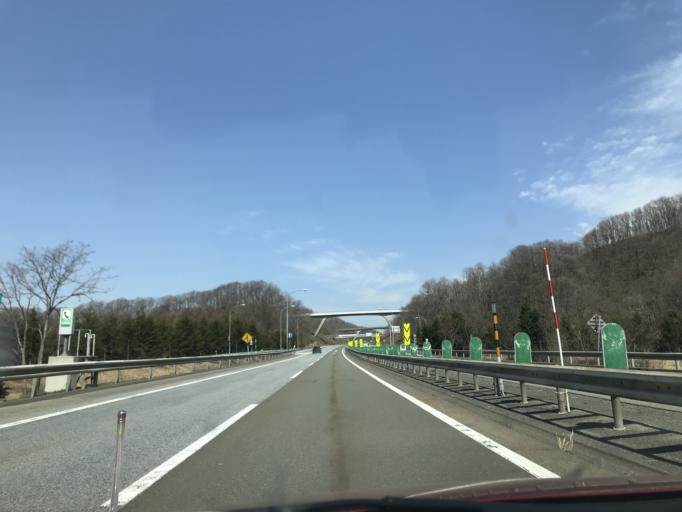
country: JP
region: Hokkaido
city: Iwamizawa
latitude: 43.2442
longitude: 141.8303
